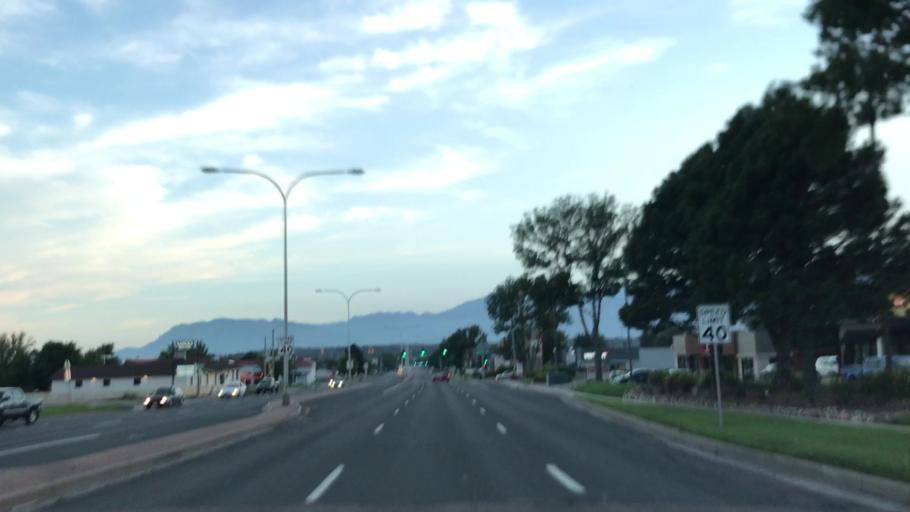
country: US
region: Colorado
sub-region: El Paso County
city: Cimarron Hills
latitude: 38.8966
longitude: -104.7484
